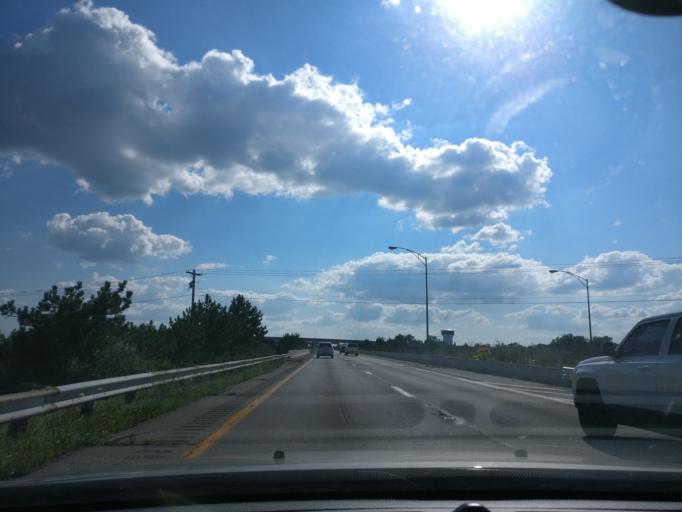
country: US
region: Ohio
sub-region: Montgomery County
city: West Carrollton City
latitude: 39.6245
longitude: -84.2255
